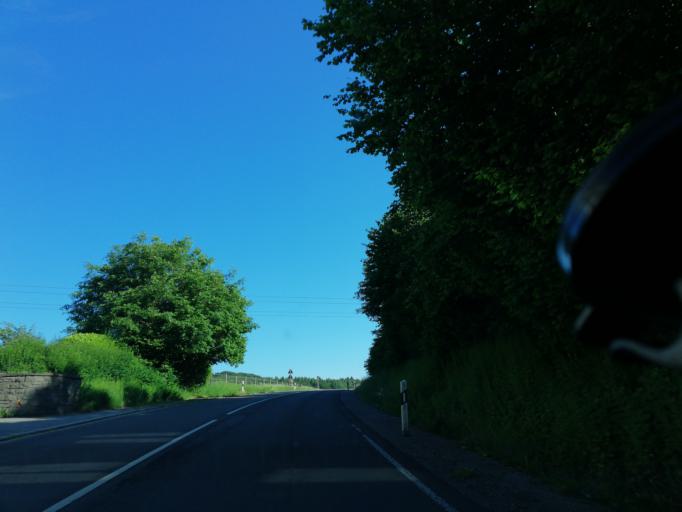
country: DE
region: North Rhine-Westphalia
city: Gevelsberg
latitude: 51.3395
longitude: 7.3056
